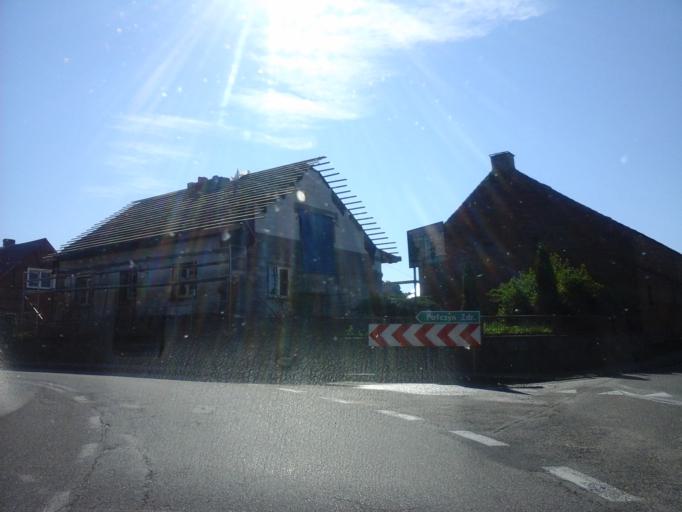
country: PL
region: West Pomeranian Voivodeship
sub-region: Powiat drawski
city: Zlocieniec
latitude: 53.6380
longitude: 15.9733
